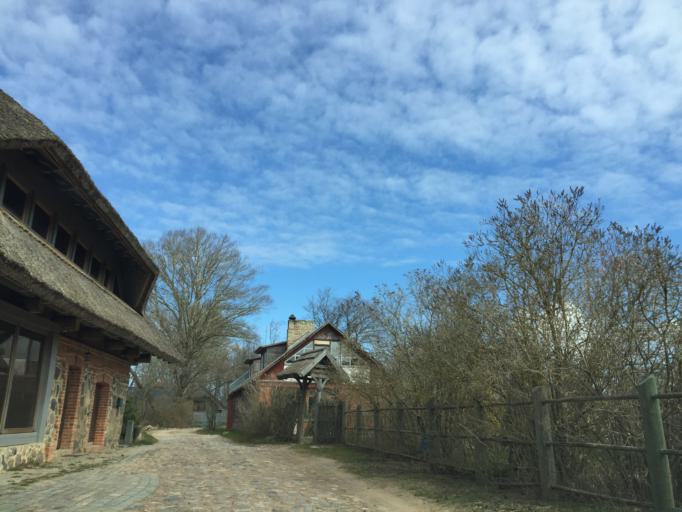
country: LV
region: Salacgrivas
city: Salacgriva
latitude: 57.6089
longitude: 24.3827
